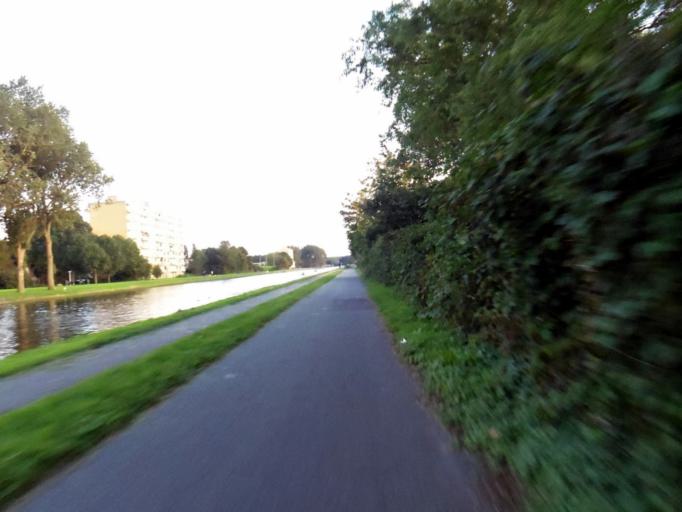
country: NL
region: South Holland
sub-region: Gemeente Voorschoten
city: Voorschoten
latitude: 52.1458
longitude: 4.4658
